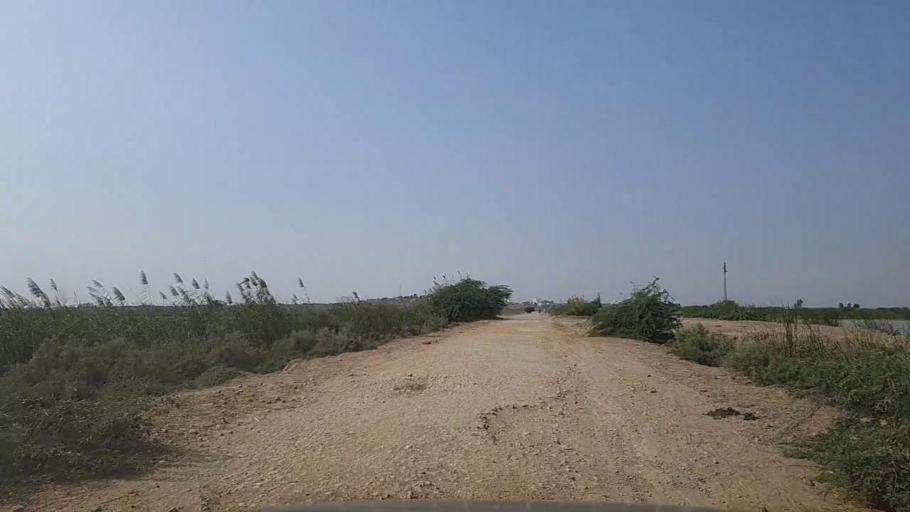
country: PK
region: Sindh
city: Chuhar Jamali
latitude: 24.5478
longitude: 67.8992
